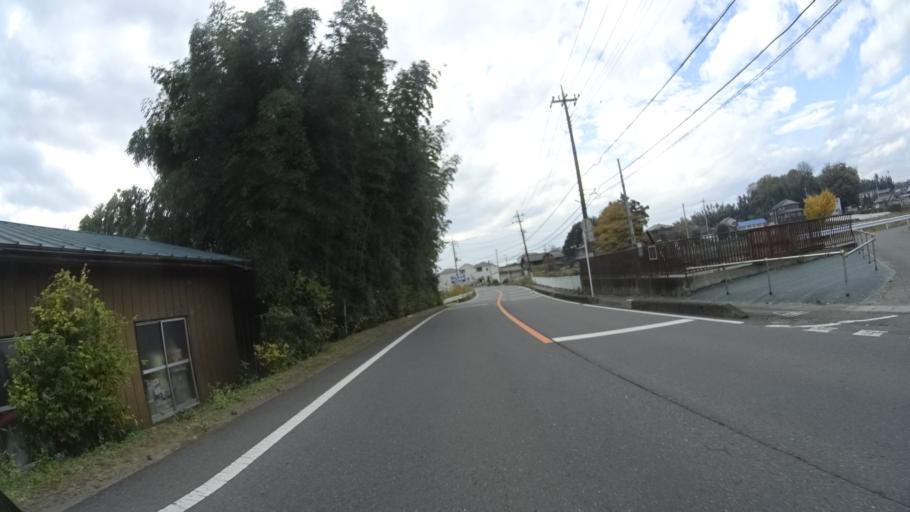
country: JP
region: Gunma
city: Maebashi-shi
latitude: 36.4109
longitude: 139.1403
